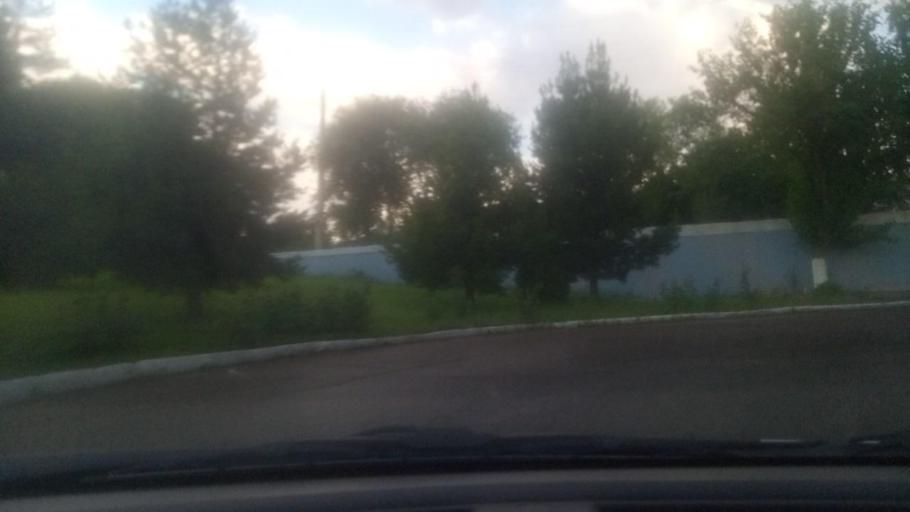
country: UZ
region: Toshkent Shahri
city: Tashkent
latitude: 41.3177
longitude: 69.1924
